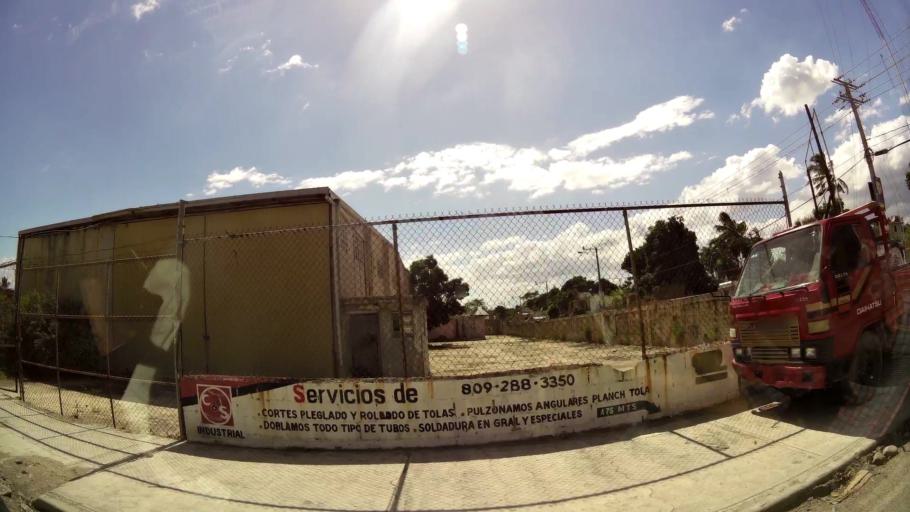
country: DO
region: San Cristobal
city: San Cristobal
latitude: 18.4244
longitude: -70.0987
